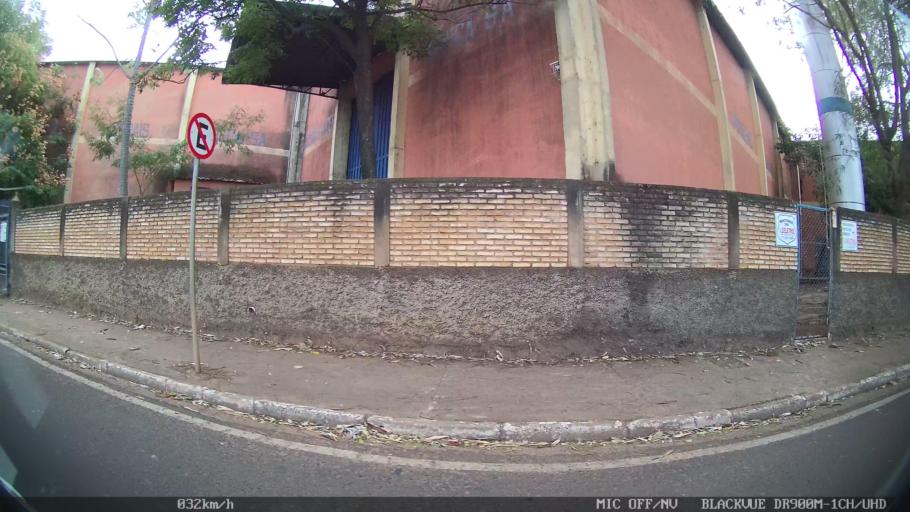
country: BR
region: Sao Paulo
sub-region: Catanduva
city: Catanduva
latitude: -21.1264
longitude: -48.9824
